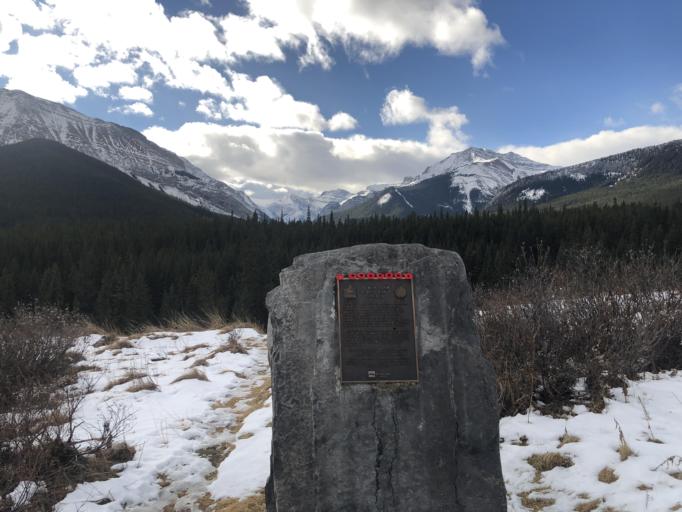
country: CA
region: Alberta
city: Canmore
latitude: 50.9154
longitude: -114.9195
